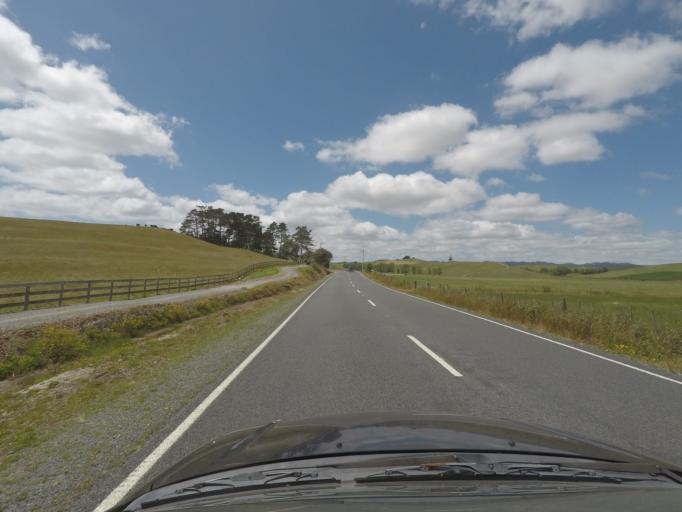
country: NZ
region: Northland
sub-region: Whangarei
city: Ruakaka
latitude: -35.9920
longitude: 174.4610
